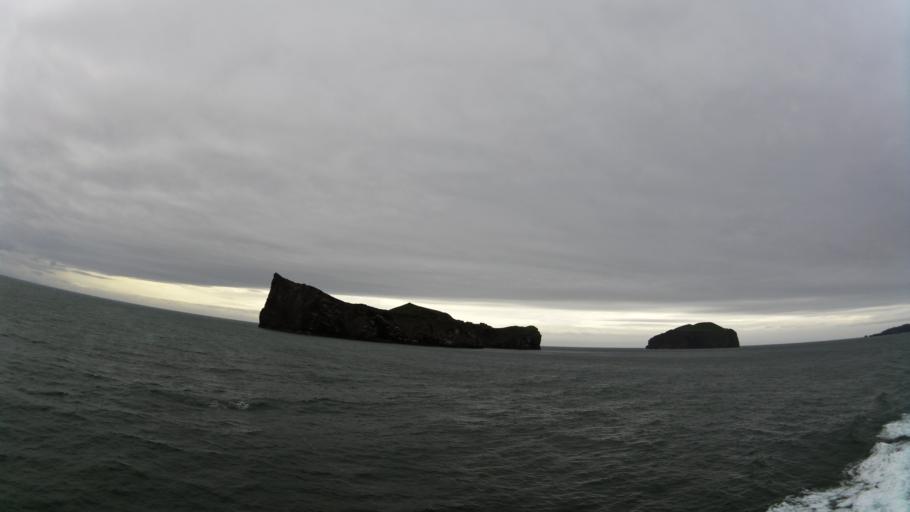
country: IS
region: South
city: Vestmannaeyjar
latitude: 63.4750
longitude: -20.1935
